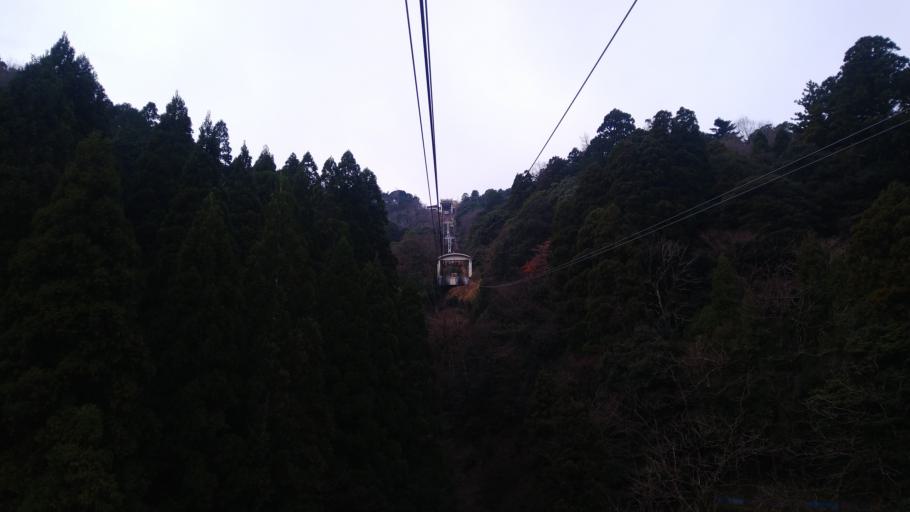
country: JP
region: Hyogo
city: Toyooka
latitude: 35.6247
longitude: 134.8026
